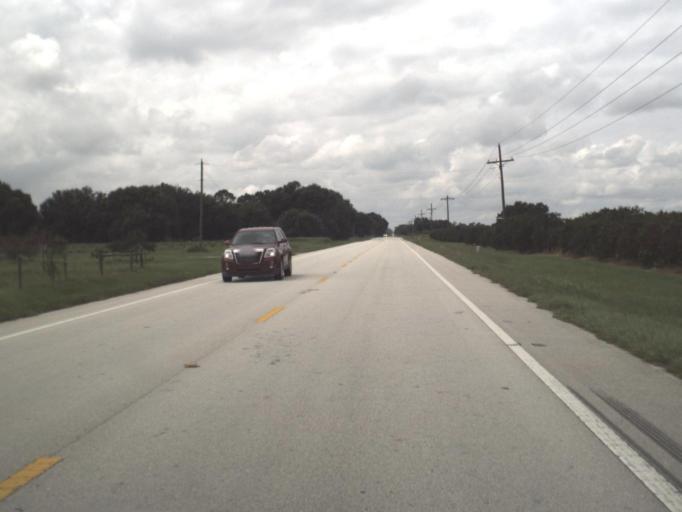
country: US
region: Florida
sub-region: Hardee County
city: Bowling Green
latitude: 27.5948
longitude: -81.8964
